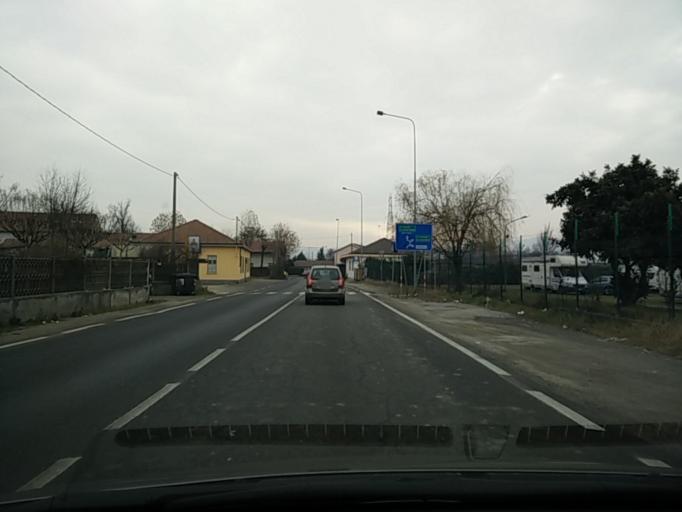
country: IT
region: Piedmont
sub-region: Provincia di Torino
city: Settimo Torinese
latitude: 45.1502
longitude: 7.7358
